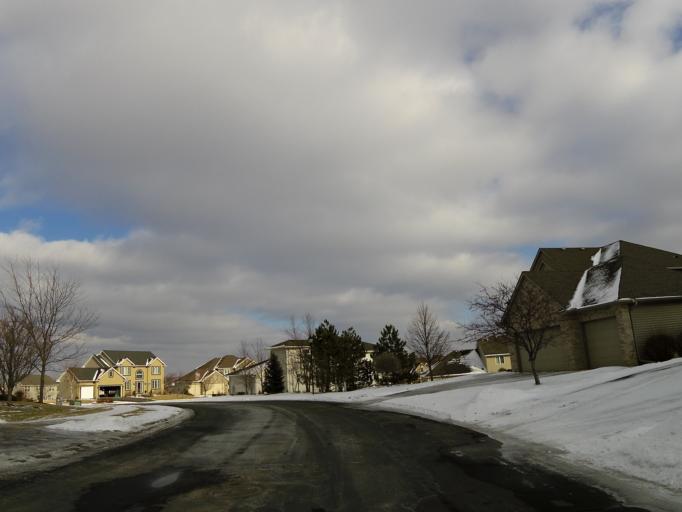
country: US
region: Minnesota
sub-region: Scott County
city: Prior Lake
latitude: 44.7272
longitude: -93.4600
